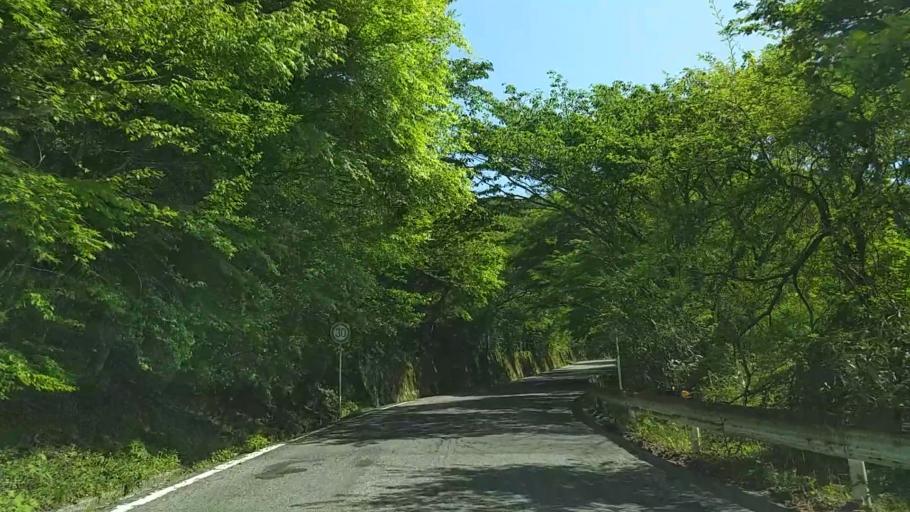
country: JP
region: Shizuoka
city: Gotemba
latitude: 35.2746
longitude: 138.9614
